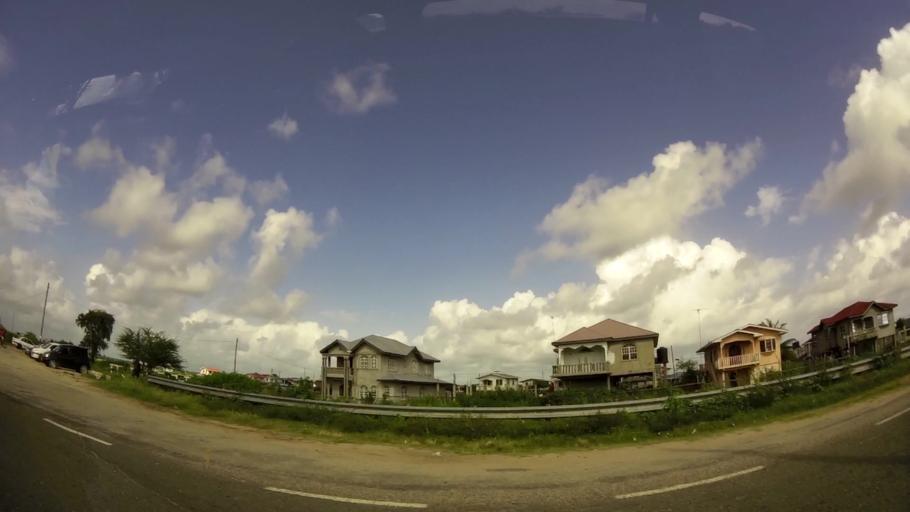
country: GY
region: Demerara-Mahaica
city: Mahaica Village
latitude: 6.7398
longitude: -57.9566
